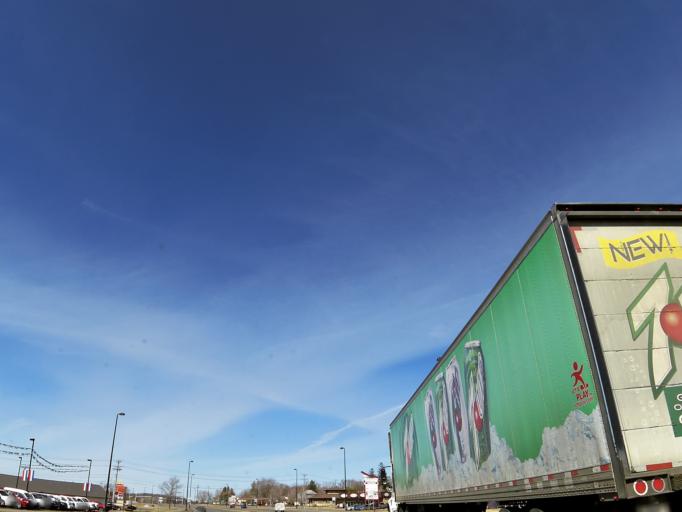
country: US
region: Minnesota
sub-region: Wright County
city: Buffalo
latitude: 45.1770
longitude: -93.8668
